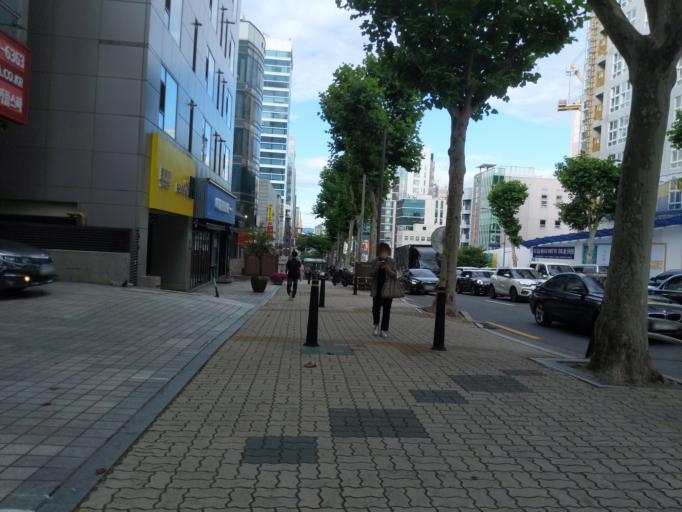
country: KR
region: Seoul
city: Seoul
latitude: 37.5068
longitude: 127.0320
